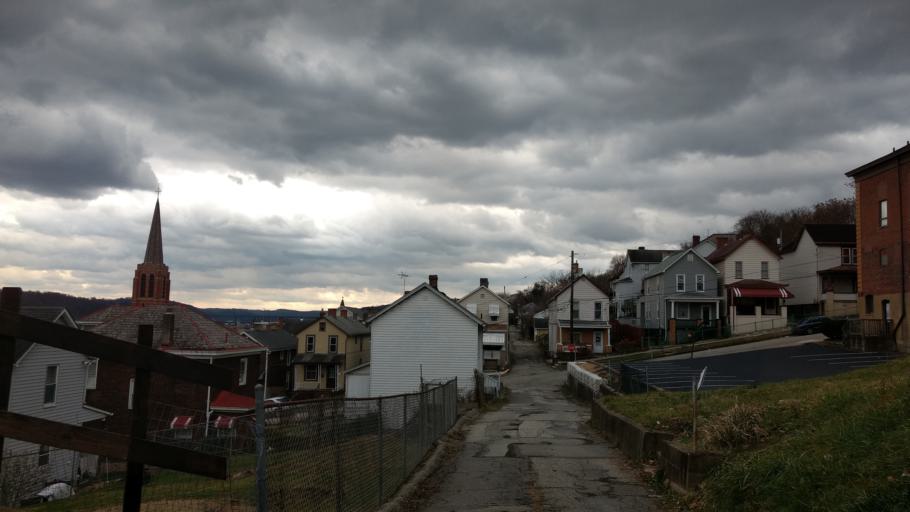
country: US
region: Pennsylvania
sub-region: Washington County
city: Charleroi
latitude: 40.1404
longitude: -79.9031
